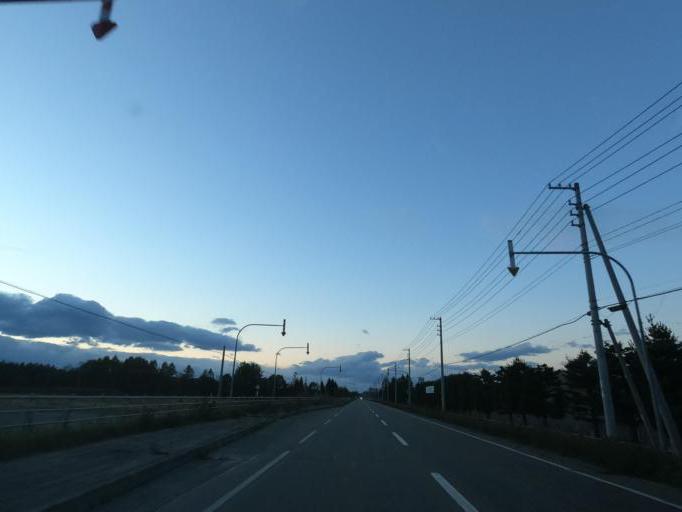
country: JP
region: Hokkaido
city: Obihiro
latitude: 42.6616
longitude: 143.1807
